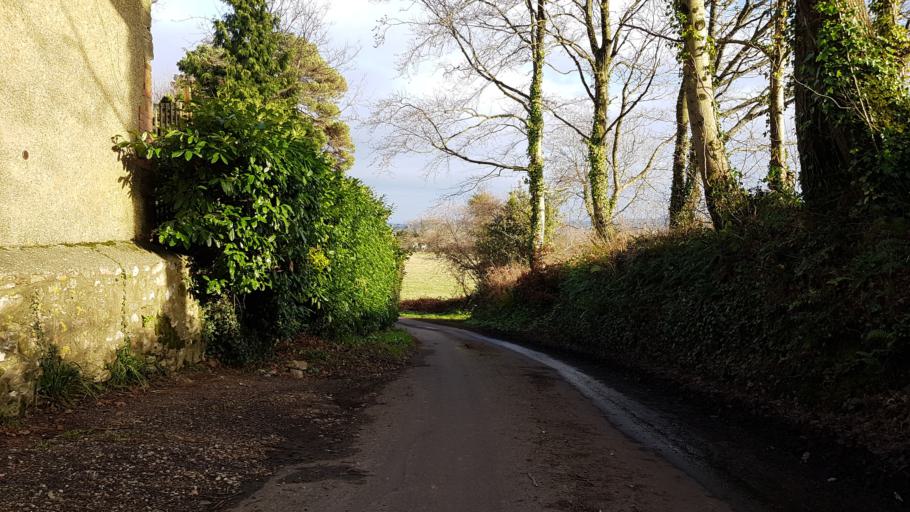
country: GB
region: England
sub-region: Somerset
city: Chard
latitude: 50.9121
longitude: -2.9802
